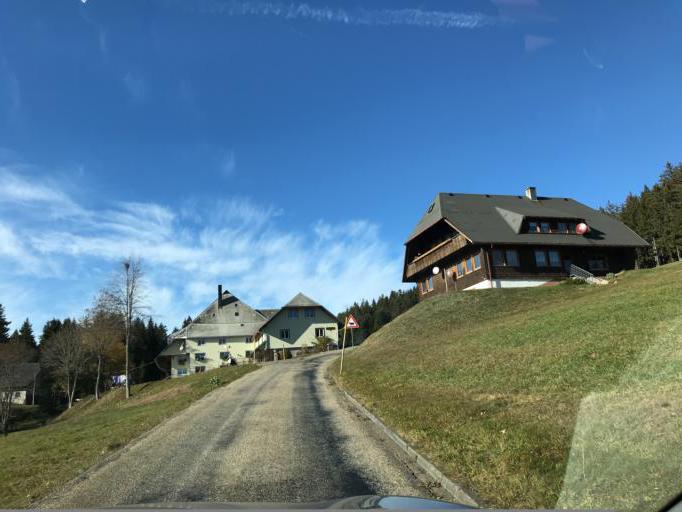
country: DE
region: Baden-Wuerttemberg
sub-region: Freiburg Region
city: Schonwald im Schwarzwald
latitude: 48.0904
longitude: 8.1693
